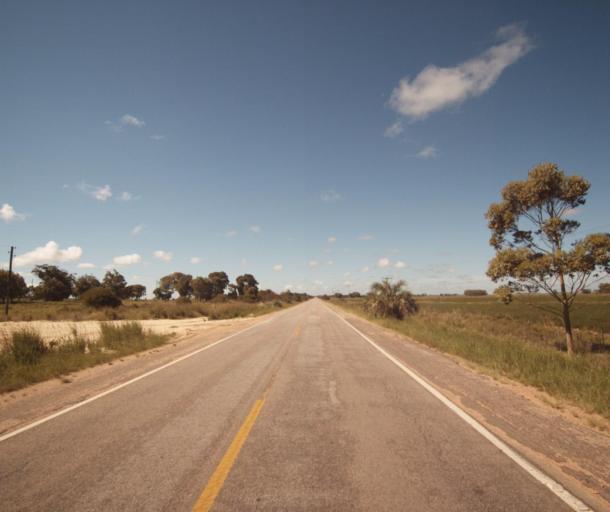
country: BR
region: Rio Grande do Sul
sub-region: Chui
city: Chui
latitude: -33.6455
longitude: -53.4249
